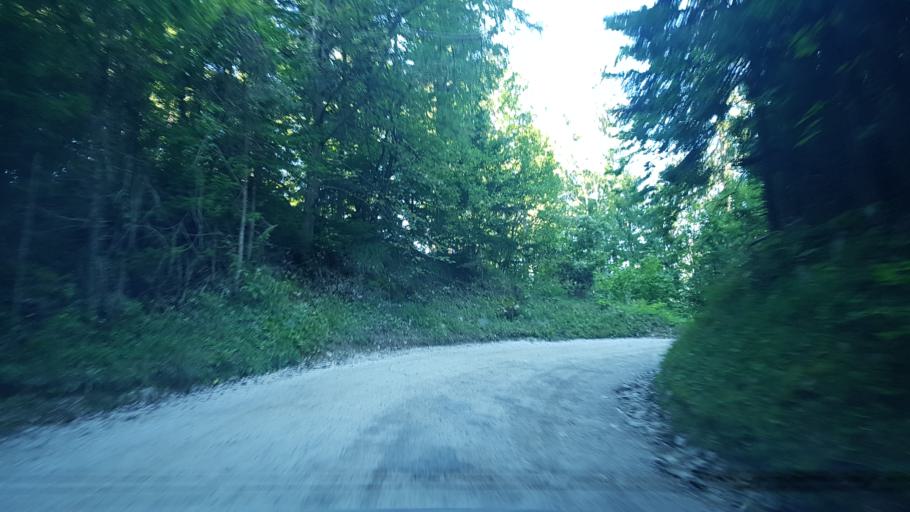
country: SI
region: Ravne na Koroskem
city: Kotlje
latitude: 46.5063
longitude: 14.9539
